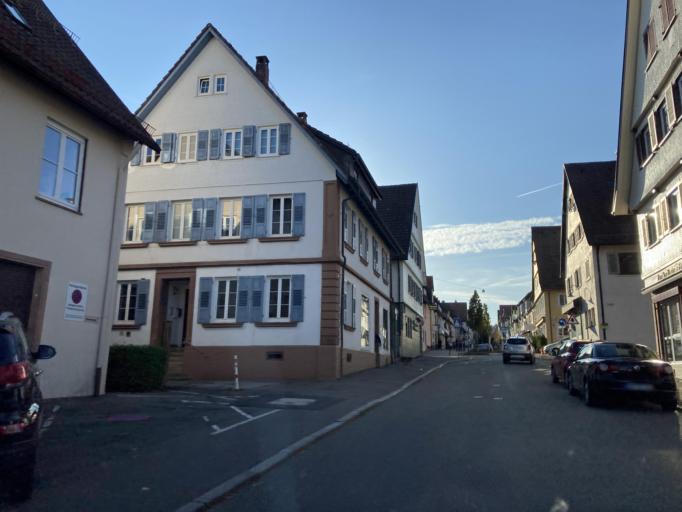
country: DE
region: Baden-Wuerttemberg
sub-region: Karlsruhe Region
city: Freudenstadt
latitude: 48.4632
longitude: 8.4154
